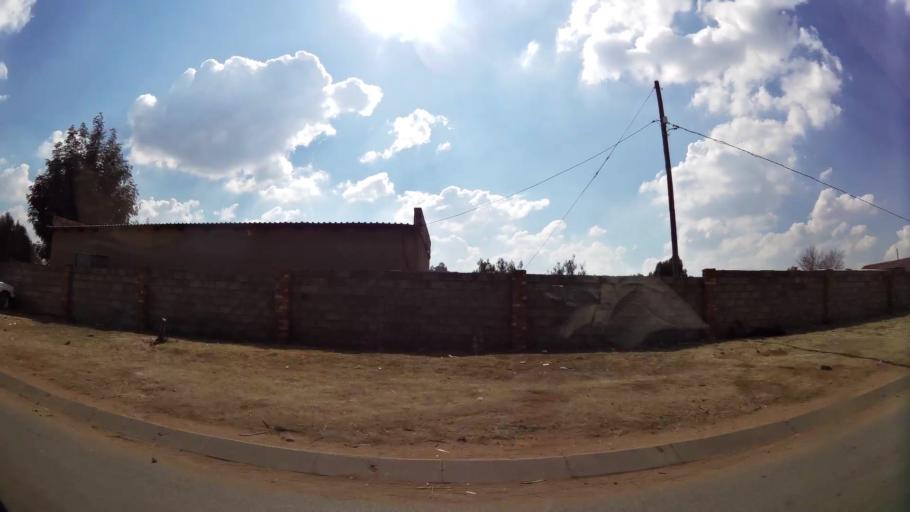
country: ZA
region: Gauteng
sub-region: City of Johannesburg Metropolitan Municipality
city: Roodepoort
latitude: -26.1900
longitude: 27.8694
